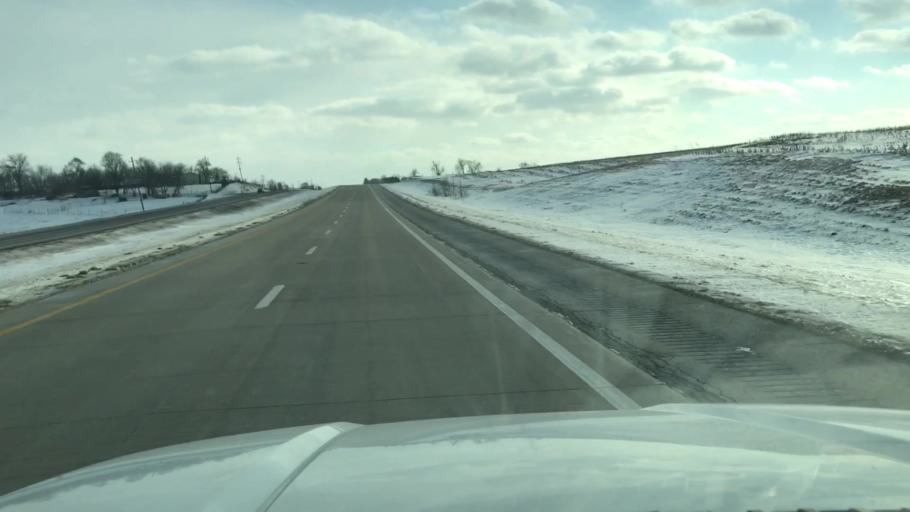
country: US
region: Missouri
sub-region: Nodaway County
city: Maryville
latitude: 40.2225
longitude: -94.8682
